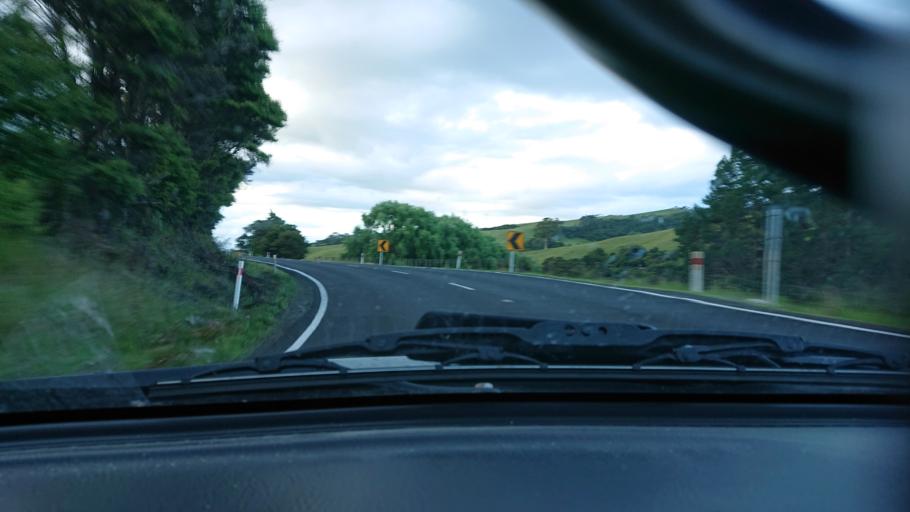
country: NZ
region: Auckland
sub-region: Auckland
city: Parakai
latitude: -36.4600
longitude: 174.4452
